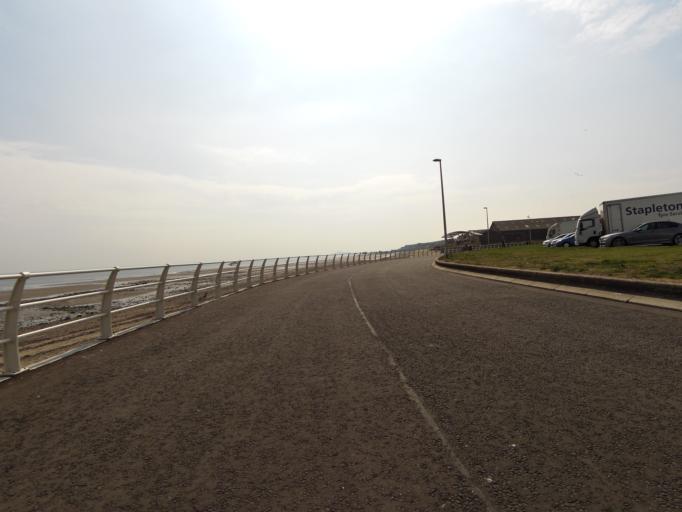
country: GB
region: Scotland
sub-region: Fife
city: Kirkcaldy
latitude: 56.1002
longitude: -3.1599
